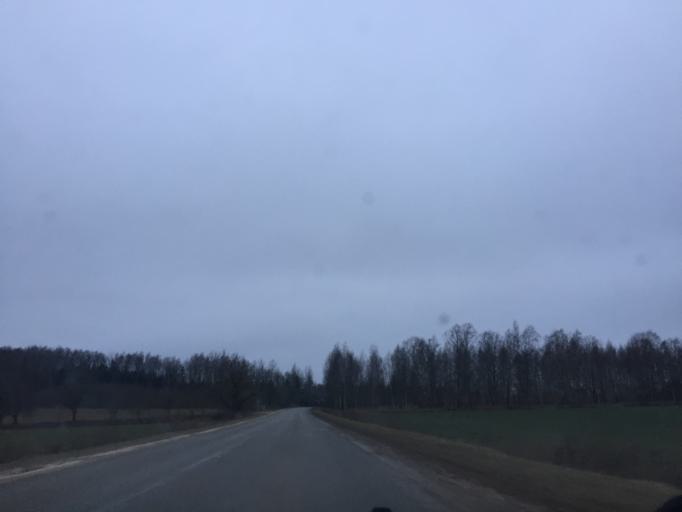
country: LV
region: Raunas
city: Rauna
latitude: 57.3392
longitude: 25.5767
